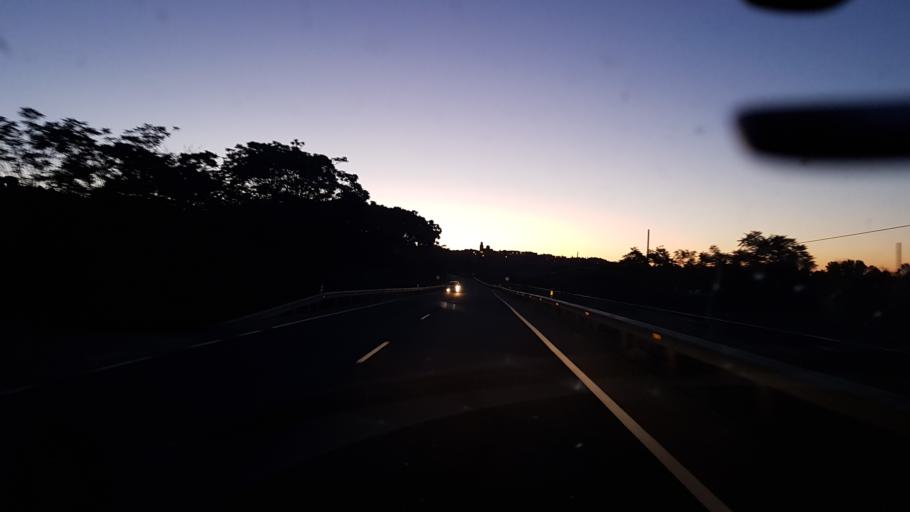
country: ES
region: Castille and Leon
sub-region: Provincia de Zamora
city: Toro
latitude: 41.5125
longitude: -5.4228
